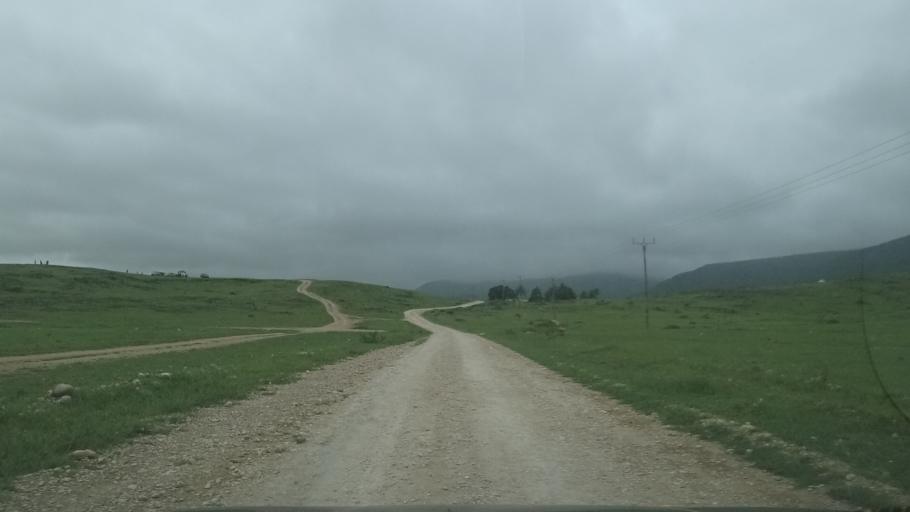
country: OM
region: Zufar
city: Salalah
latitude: 17.1163
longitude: 54.2319
